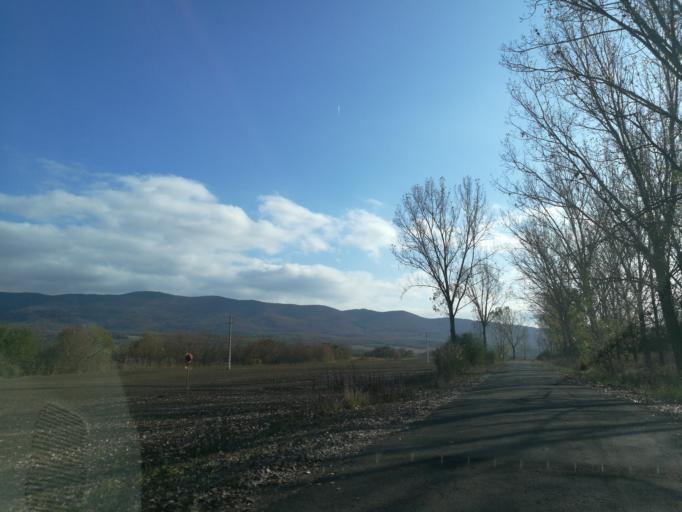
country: HU
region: Nograd
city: Paszto
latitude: 47.9024
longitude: 19.6883
